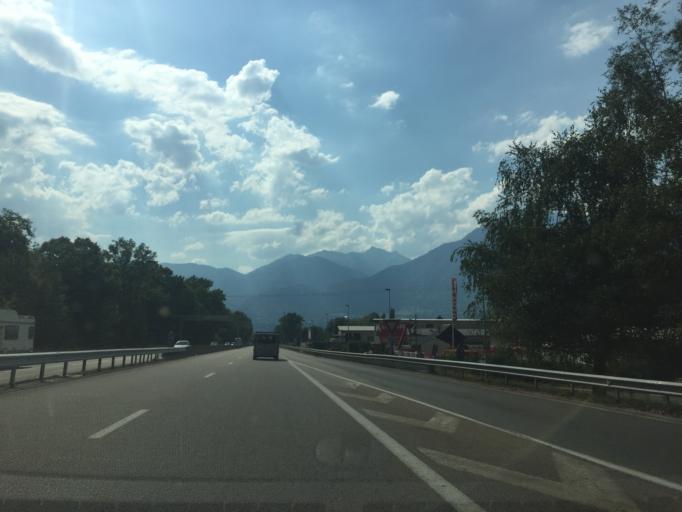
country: FR
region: Rhone-Alpes
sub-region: Departement de la Savoie
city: Albertville
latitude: 45.6625
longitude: 6.4068
